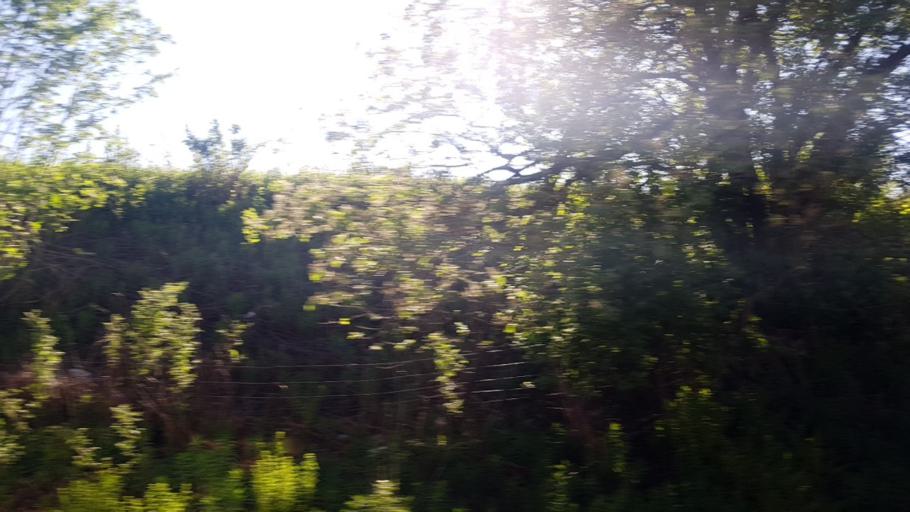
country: NO
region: Sor-Trondelag
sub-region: Melhus
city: Melhus
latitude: 63.3225
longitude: 10.3224
